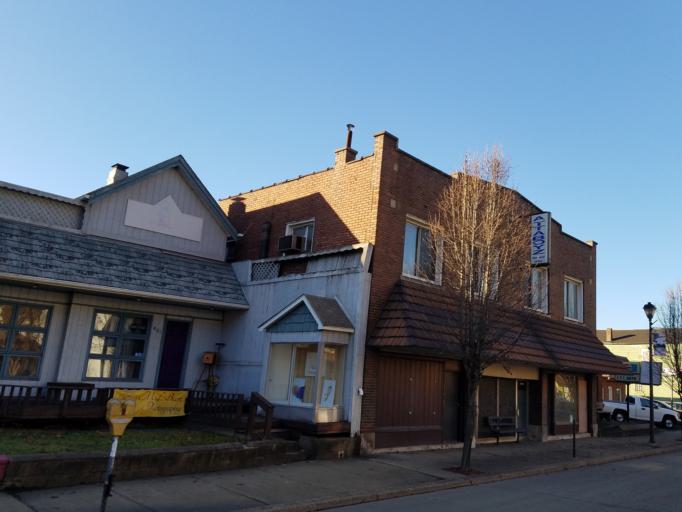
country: US
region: West Virginia
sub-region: Brooke County
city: Follansbee
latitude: 40.3262
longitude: -80.5957
